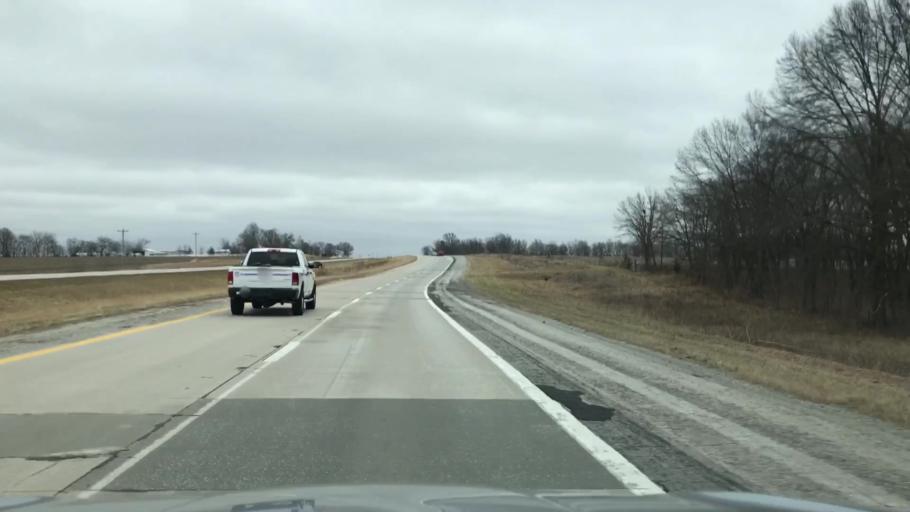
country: US
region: Missouri
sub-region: Linn County
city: Linneus
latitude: 39.7776
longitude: -93.3556
